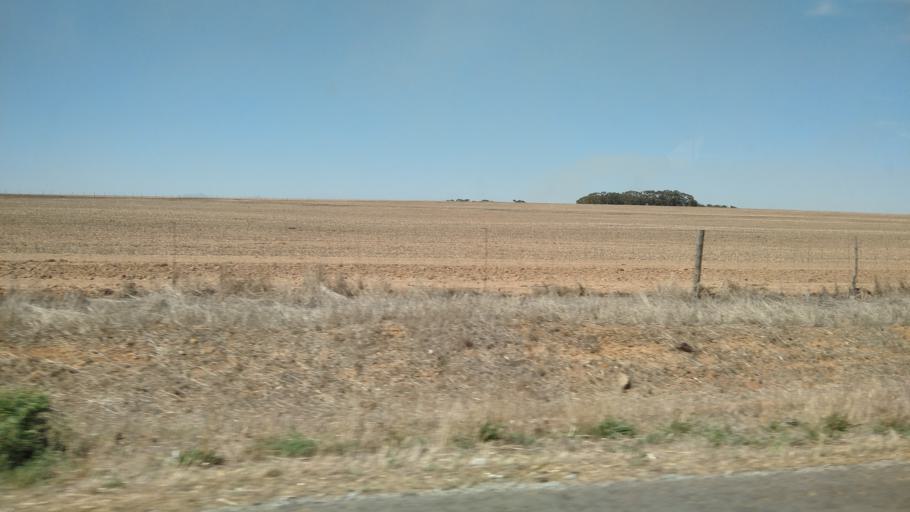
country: ZA
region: Western Cape
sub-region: West Coast District Municipality
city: Malmesbury
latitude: -33.3335
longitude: 18.6326
